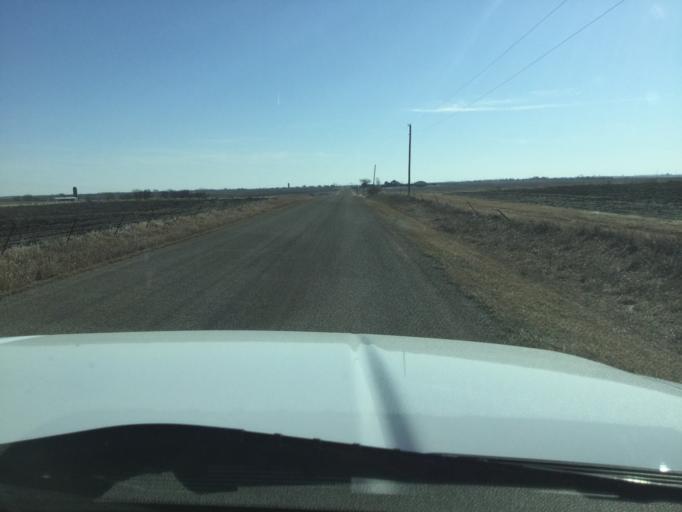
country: US
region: Kansas
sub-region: Brown County
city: Horton
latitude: 39.7254
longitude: -95.4828
